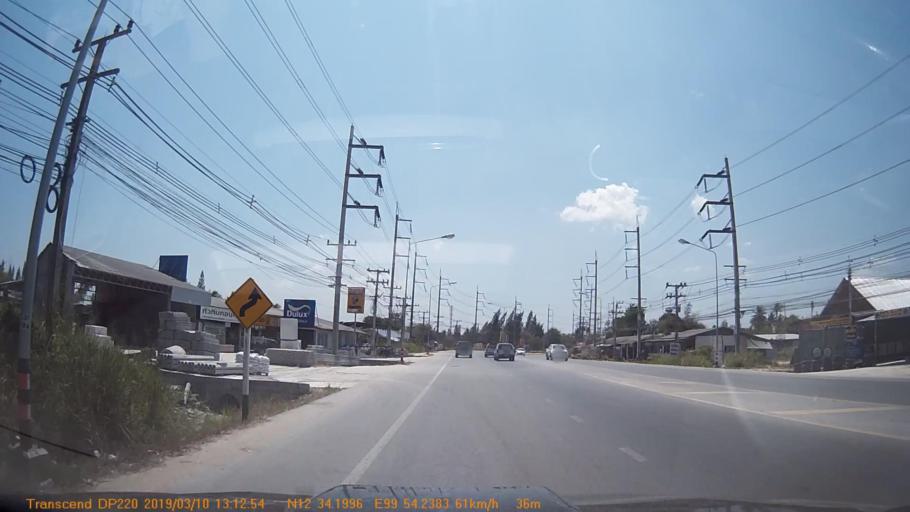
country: TH
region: Prachuap Khiri Khan
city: Hua Hin
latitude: 12.5699
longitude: 99.9039
